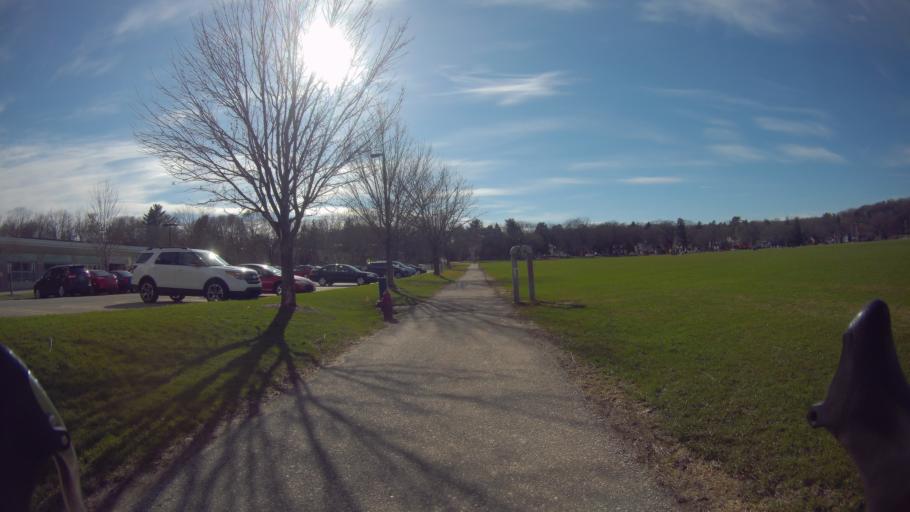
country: US
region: Wisconsin
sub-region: Dane County
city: Shorewood Hills
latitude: 43.0790
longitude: -89.4342
